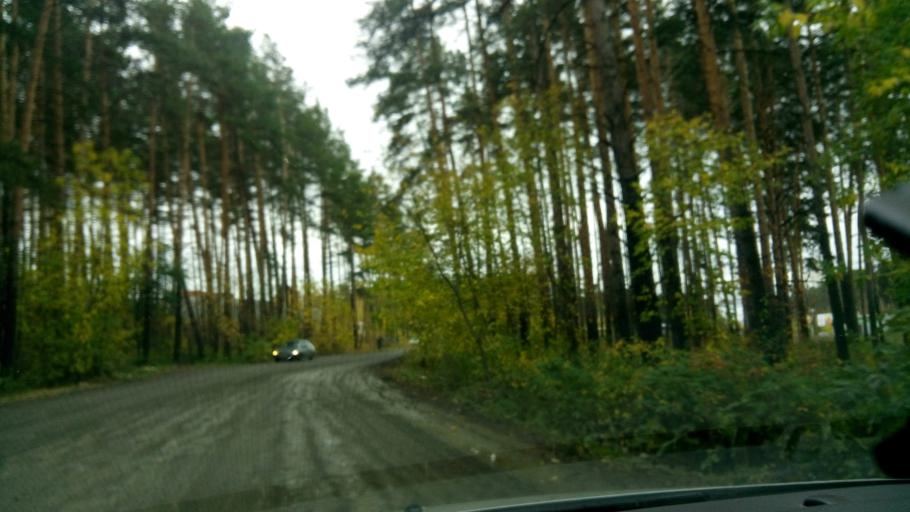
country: RU
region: Sverdlovsk
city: Shirokaya Rechka
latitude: 56.8177
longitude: 60.5232
